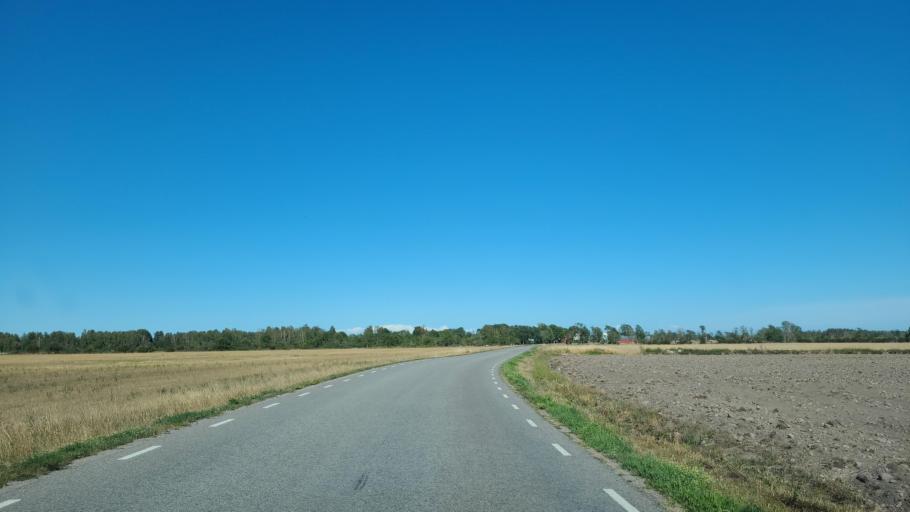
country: SE
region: Kalmar
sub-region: Borgholms Kommun
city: Borgholm
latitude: 56.9733
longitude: 16.8506
